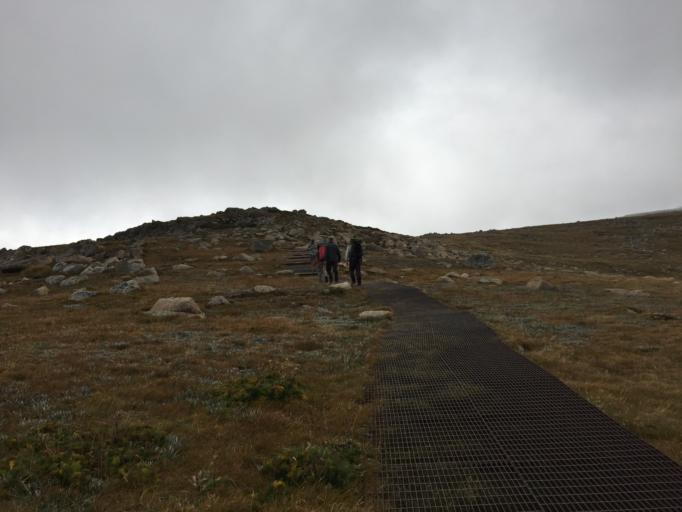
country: AU
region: New South Wales
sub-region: Snowy River
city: Jindabyne
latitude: -36.4671
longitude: 148.2703
